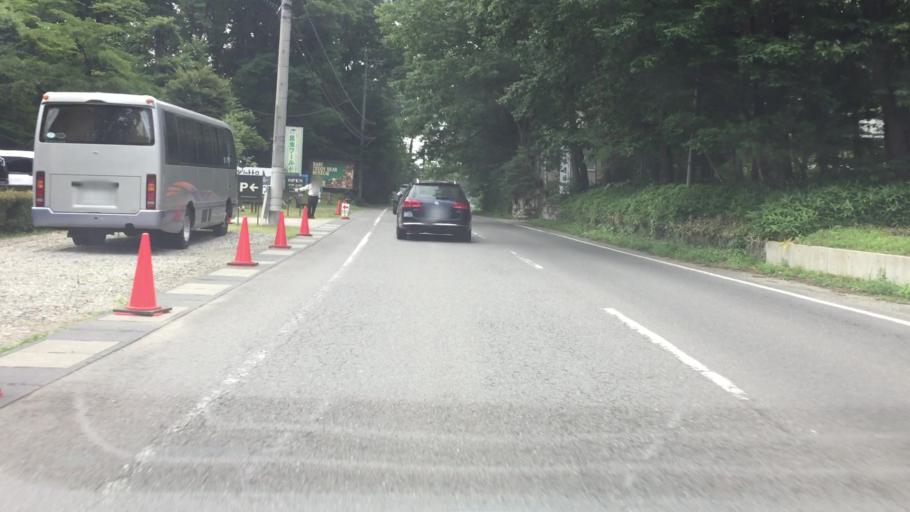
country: JP
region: Tochigi
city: Kuroiso
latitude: 37.0487
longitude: 140.0389
